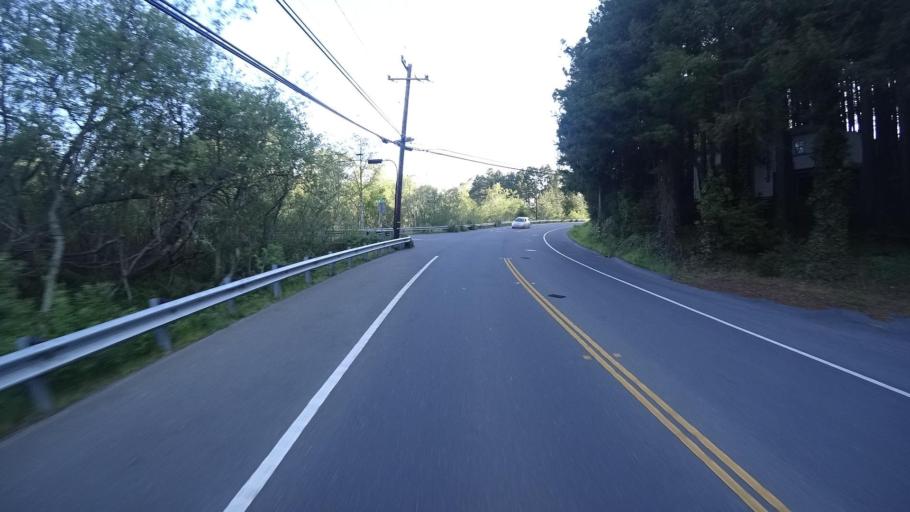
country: US
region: California
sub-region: Humboldt County
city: Bayview
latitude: 40.7695
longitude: -124.1752
